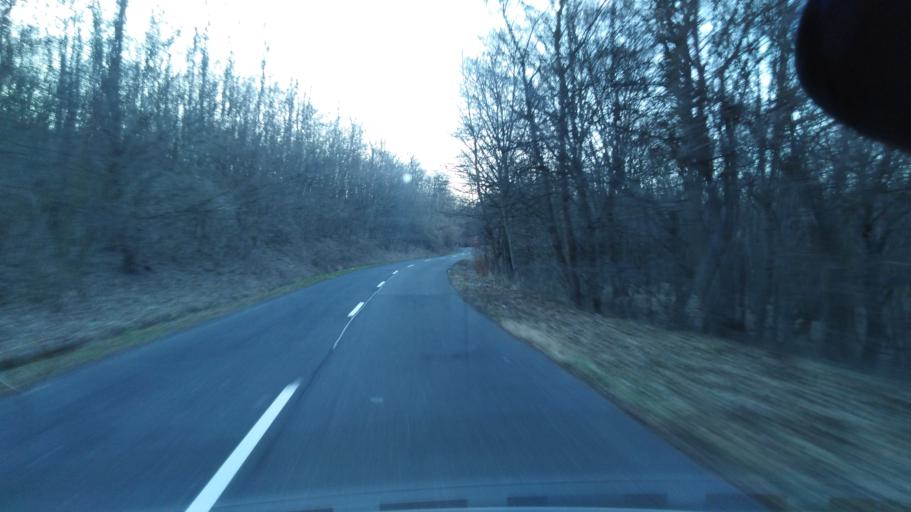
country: HU
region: Nograd
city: Salgotarjan
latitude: 48.0681
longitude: 19.8205
